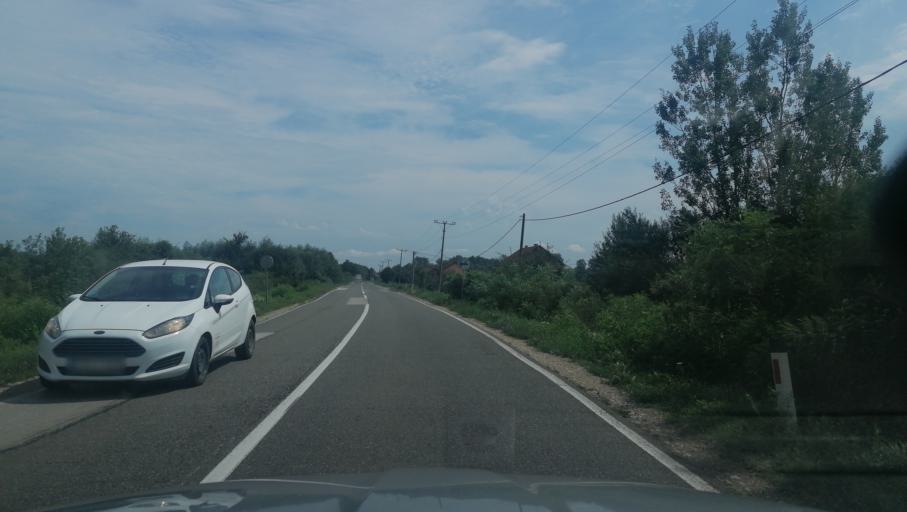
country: BA
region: Republika Srpska
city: Bosanski Samac
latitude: 45.0383
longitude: 18.5040
